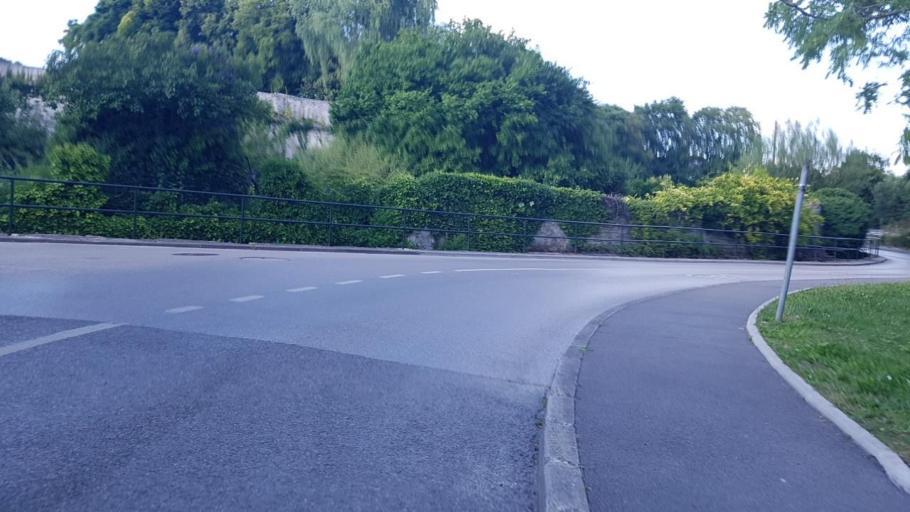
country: FR
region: Picardie
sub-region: Departement de l'Oise
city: Senlis
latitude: 49.2013
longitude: 2.5914
